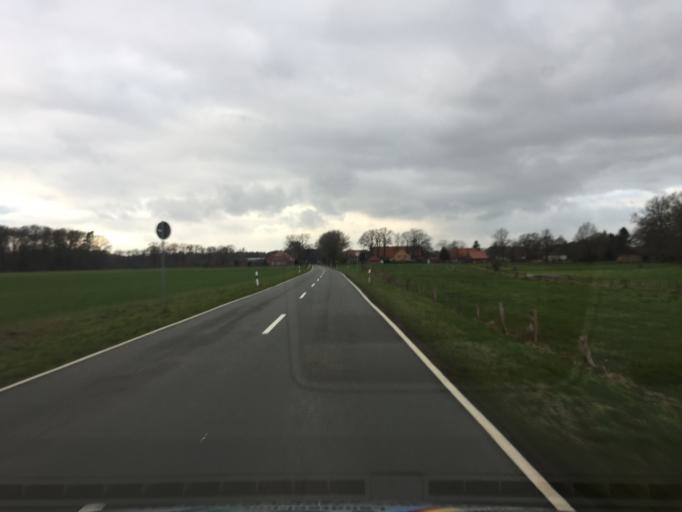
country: DE
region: Lower Saxony
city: Stolzenau
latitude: 52.5269
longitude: 9.0457
